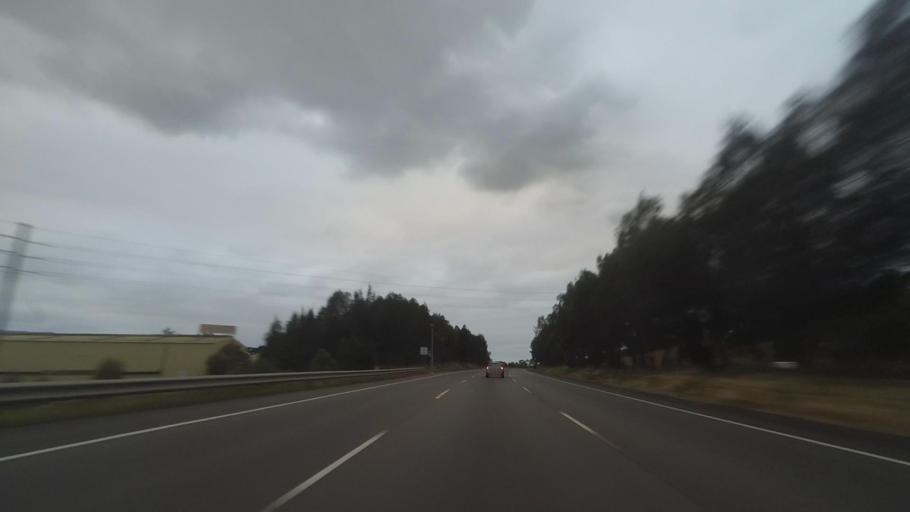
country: AU
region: New South Wales
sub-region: Wollongong
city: Berkeley
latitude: -34.4682
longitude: 150.8383
